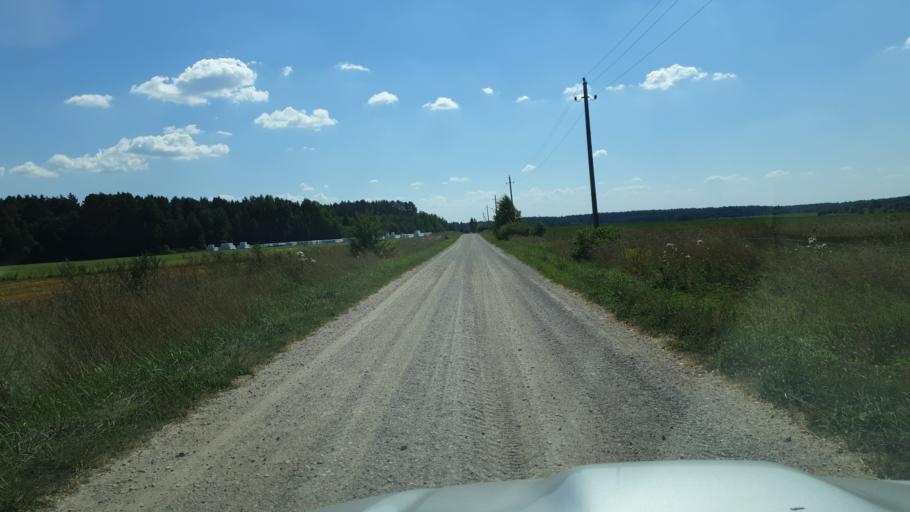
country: LT
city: Sirvintos
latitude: 54.9145
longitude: 24.9118
